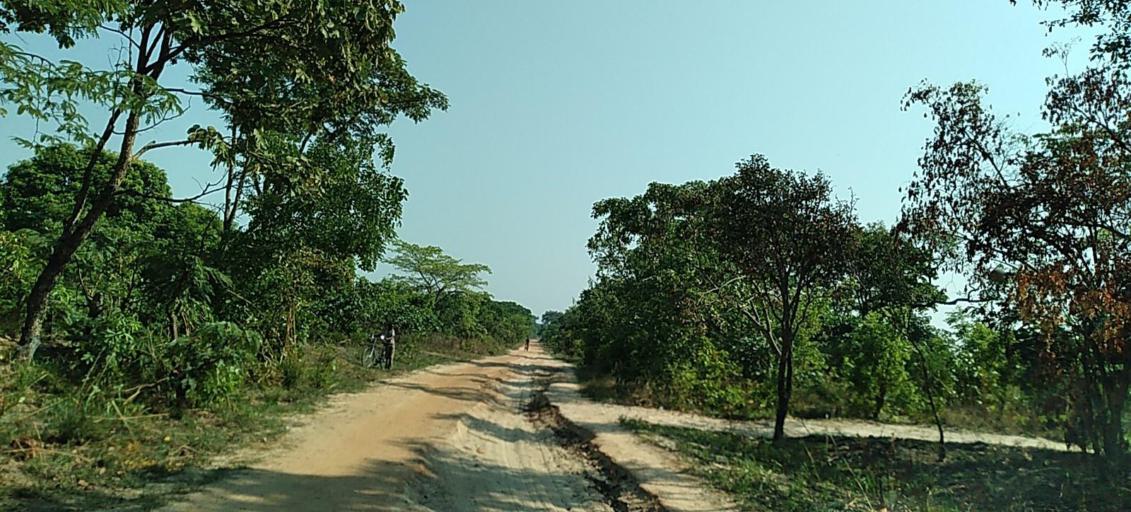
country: ZM
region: Copperbelt
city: Luanshya
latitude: -13.2875
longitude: 28.2527
